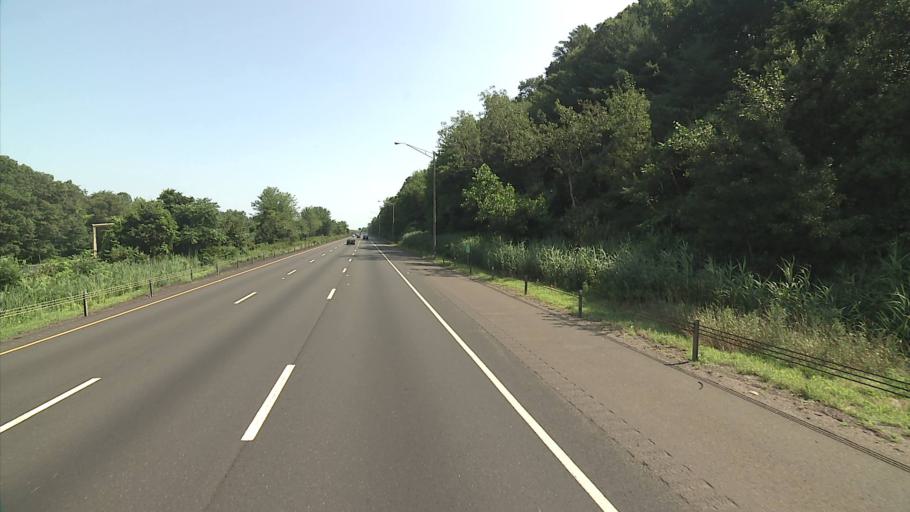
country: US
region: Connecticut
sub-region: New Haven County
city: North Haven
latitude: 41.4075
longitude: -72.8330
